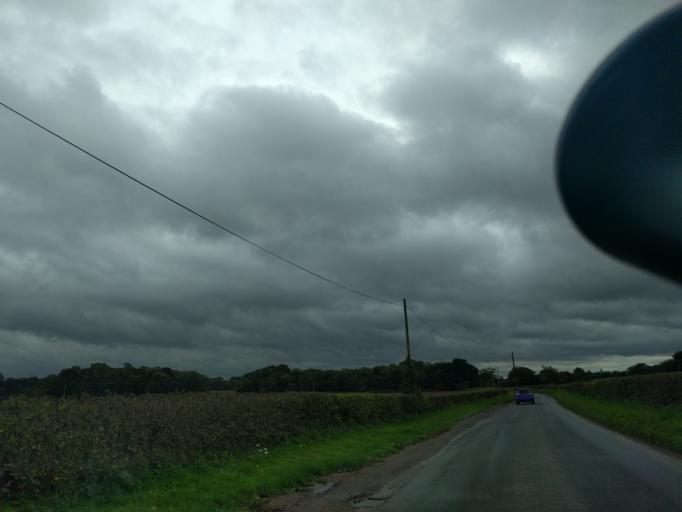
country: GB
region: England
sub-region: North Yorkshire
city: Bedale
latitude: 54.3265
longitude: -1.5666
